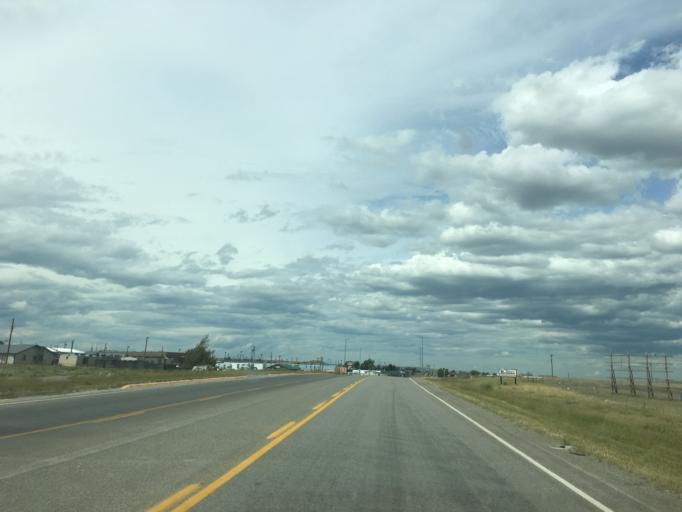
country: US
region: Montana
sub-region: Glacier County
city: South Browning
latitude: 48.5462
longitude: -113.0096
